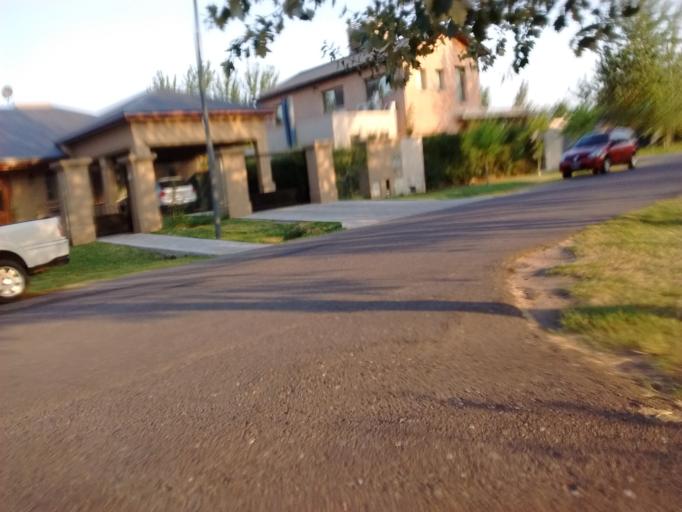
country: AR
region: Santa Fe
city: Funes
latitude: -32.9157
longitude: -60.7728
